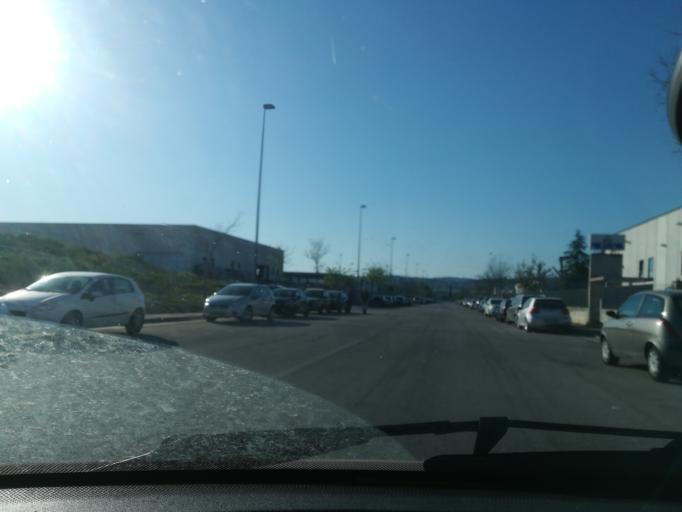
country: IT
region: The Marches
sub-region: Provincia di Macerata
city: Zona Industriale
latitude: 43.2616
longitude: 13.4859
